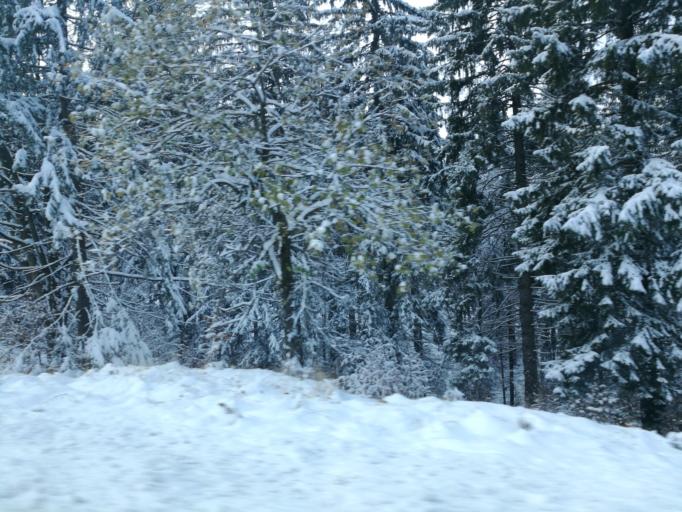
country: RO
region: Brasov
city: Brasov
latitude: 45.6046
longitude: 25.5544
